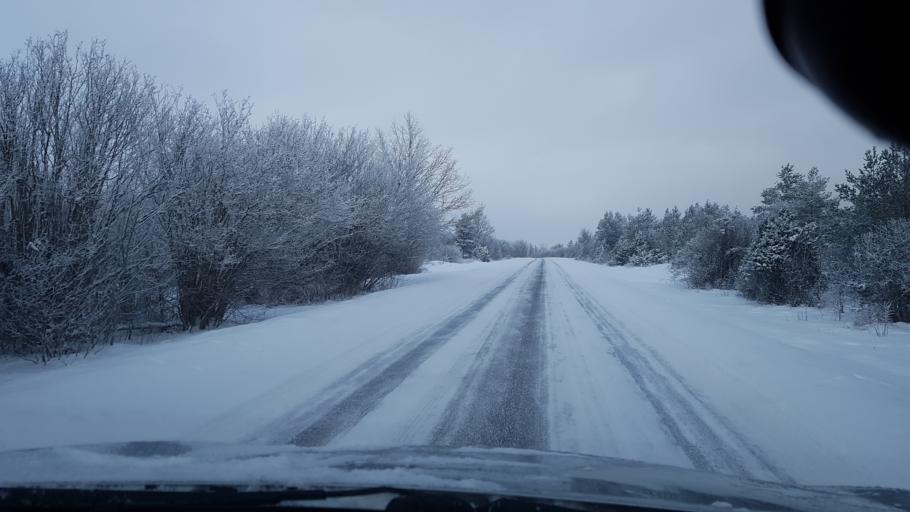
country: EE
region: Harju
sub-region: Keila linn
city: Keila
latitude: 59.3700
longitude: 24.4069
